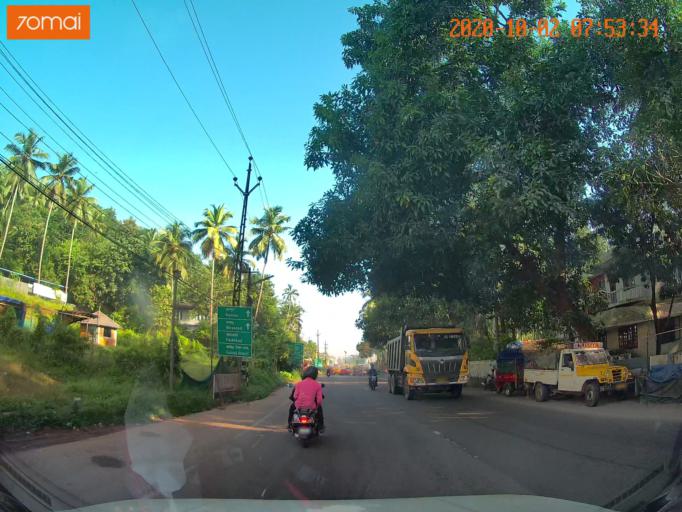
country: IN
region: Kerala
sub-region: Kozhikode
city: Ferokh
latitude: 11.1677
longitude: 75.8757
